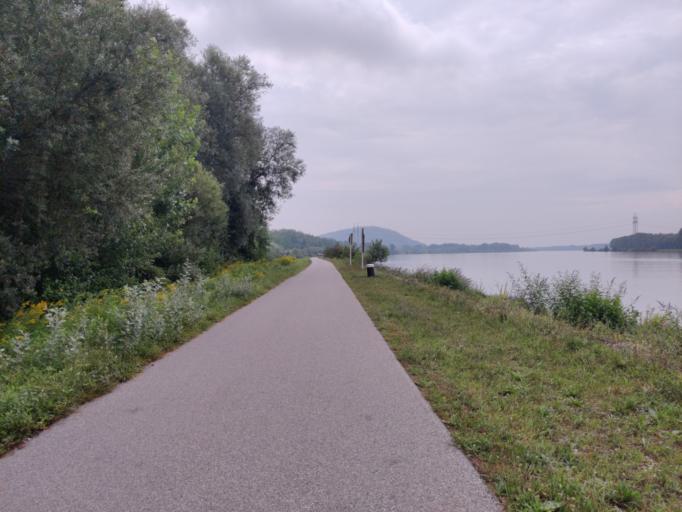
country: AT
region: Upper Austria
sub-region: Politischer Bezirk Urfahr-Umgebung
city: Steyregg
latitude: 48.2724
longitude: 14.3707
